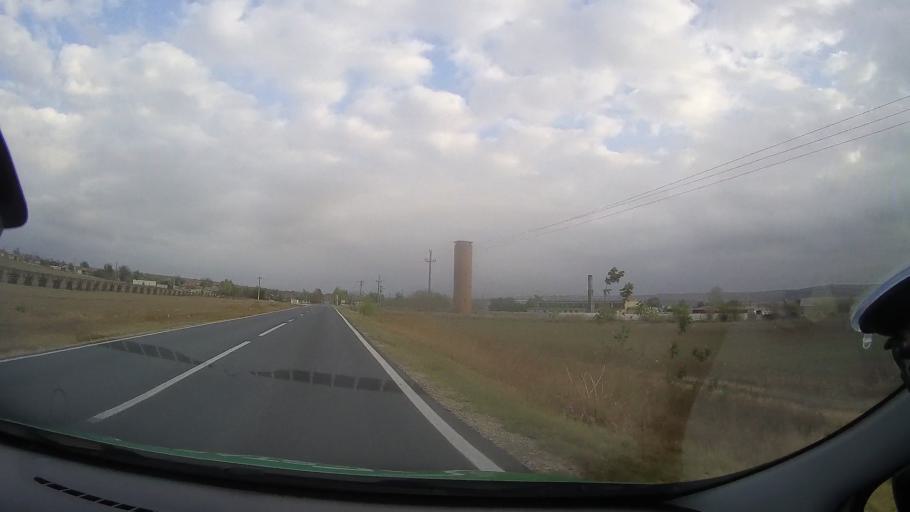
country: RO
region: Constanta
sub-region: Comuna Mircea Voda
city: Satu Nou
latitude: 44.2699
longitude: 28.2143
